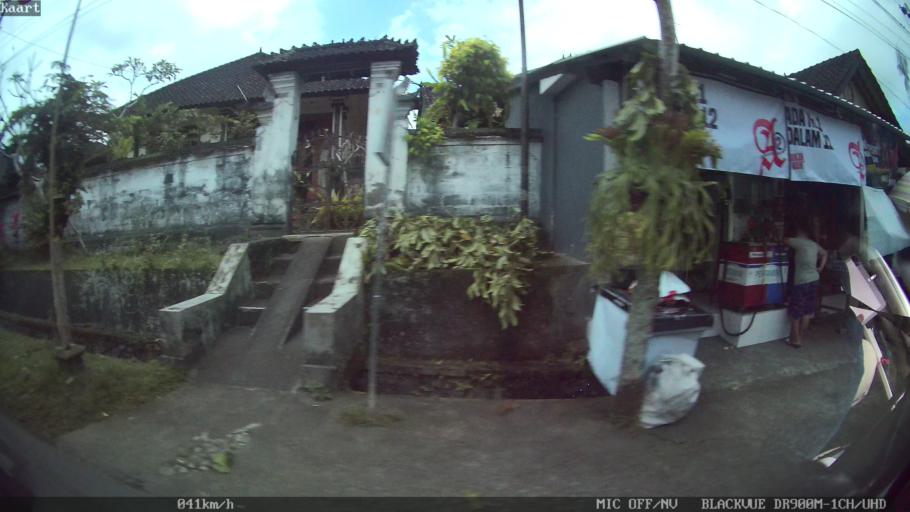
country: ID
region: Bali
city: Bangli
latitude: -8.4561
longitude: 115.3838
